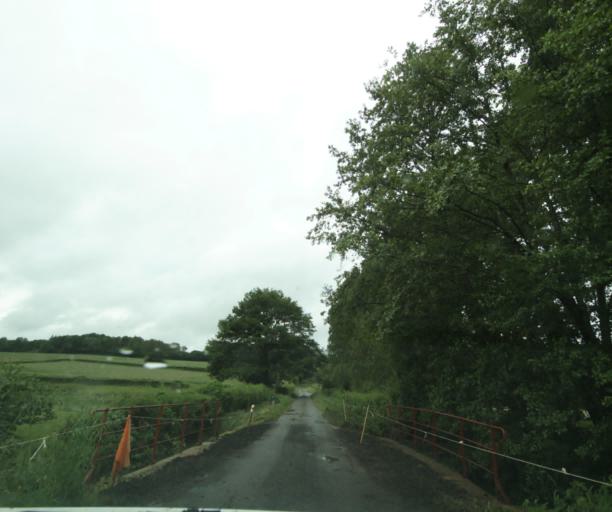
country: FR
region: Bourgogne
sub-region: Departement de Saone-et-Loire
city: Genelard
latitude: 46.5436
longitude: 4.2685
